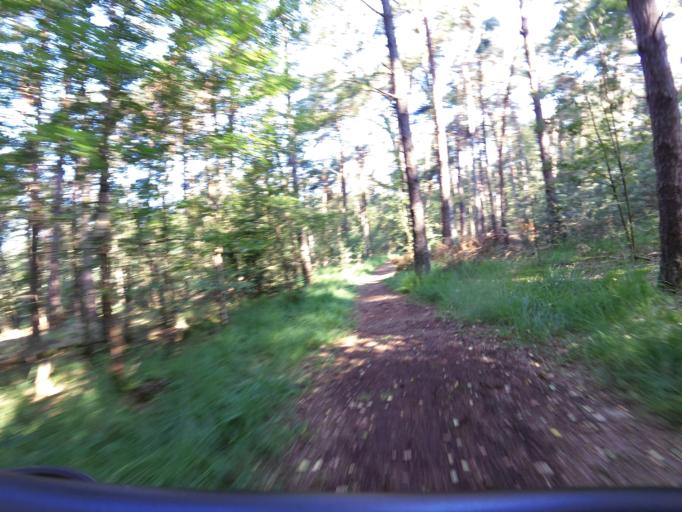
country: BE
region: Flanders
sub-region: Provincie Antwerpen
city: Kalmthout
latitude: 51.3685
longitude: 4.4508
